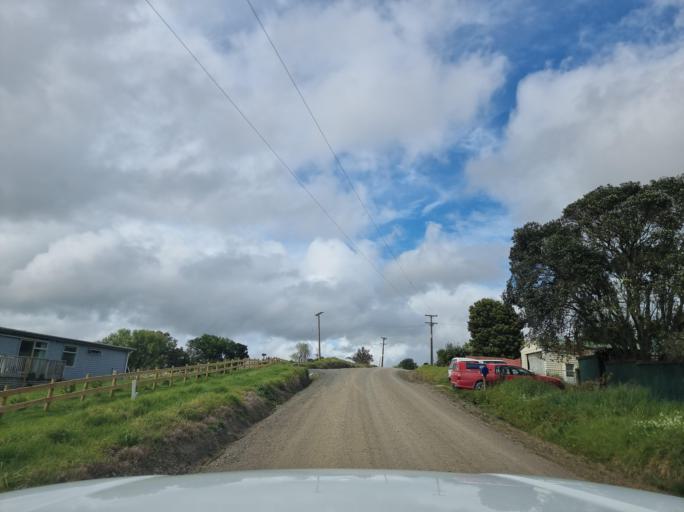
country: NZ
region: Northland
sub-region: Whangarei
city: Ruakaka
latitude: -36.1237
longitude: 174.2084
